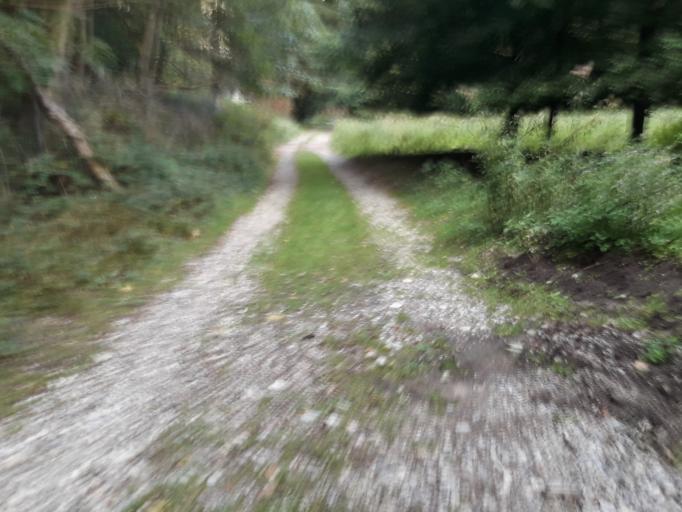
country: DE
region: North Rhine-Westphalia
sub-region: Regierungsbezirk Detmold
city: Horn
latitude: 51.8506
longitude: 8.9098
